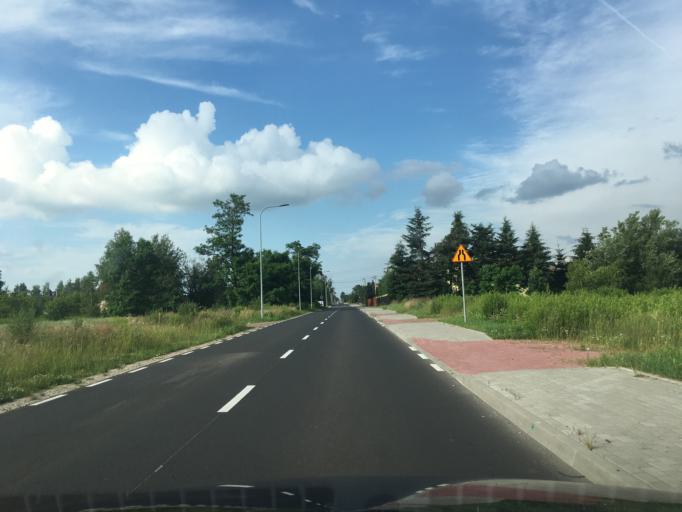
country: PL
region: Masovian Voivodeship
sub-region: Powiat wolominski
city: Radzymin
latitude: 52.4008
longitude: 21.2049
